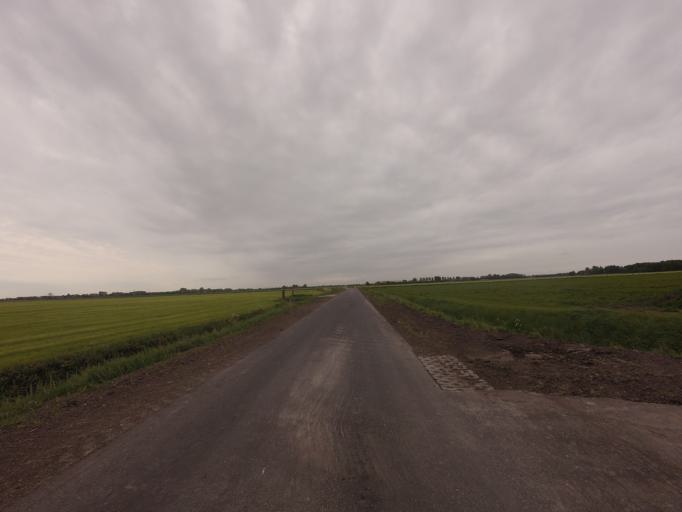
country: NL
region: Zeeland
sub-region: Gemeente Middelburg
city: Middelburg
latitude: 51.5444
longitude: 3.5453
